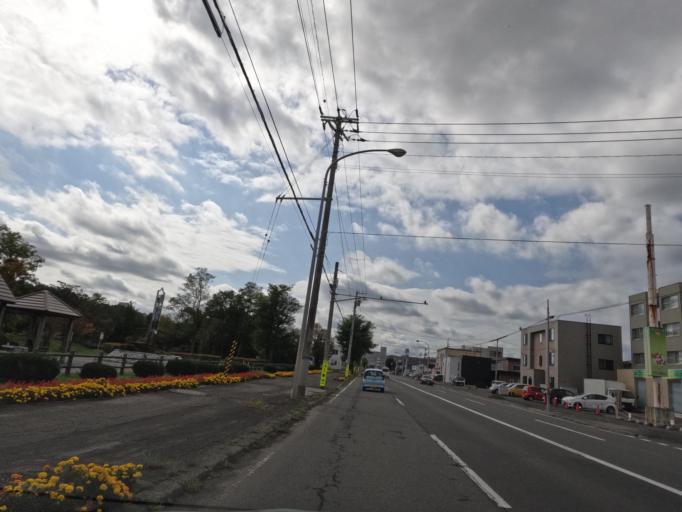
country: JP
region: Hokkaido
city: Chitose
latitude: 42.8201
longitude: 141.6552
